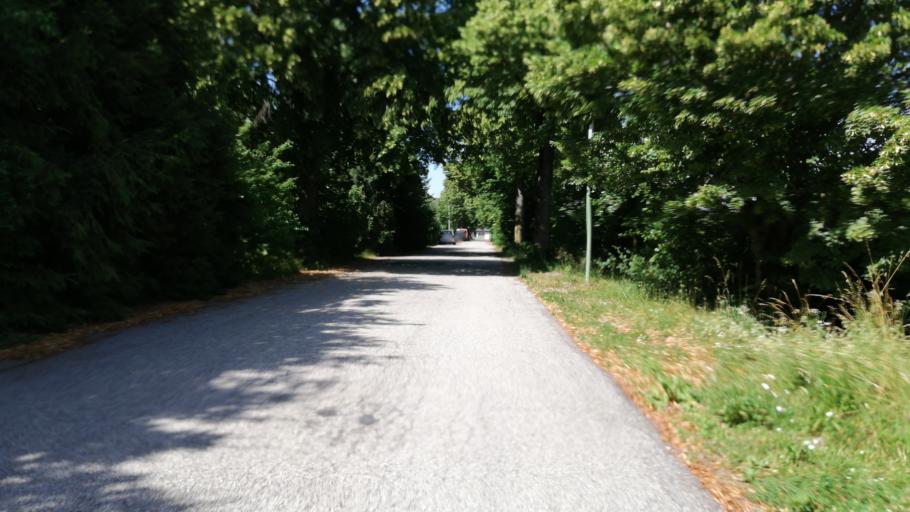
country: AT
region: Upper Austria
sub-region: Wels Stadt
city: Wels
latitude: 48.1845
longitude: 14.0291
